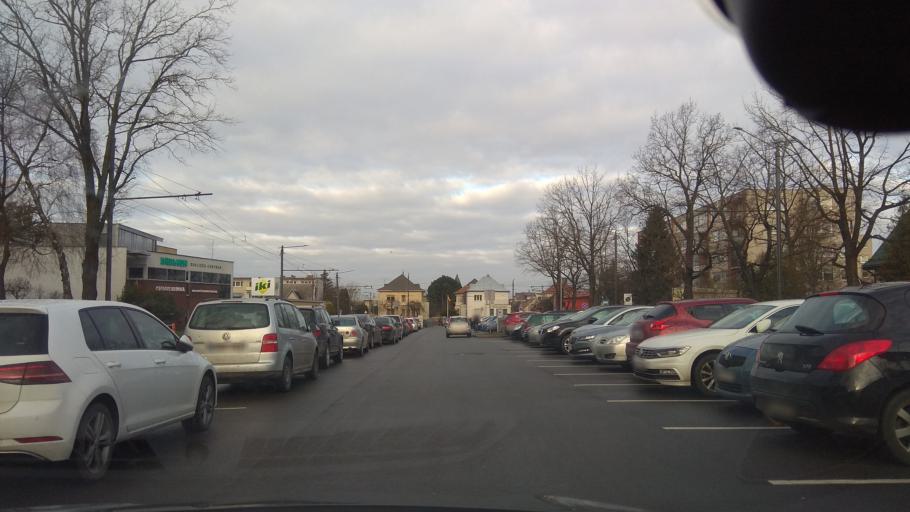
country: LT
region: Kauno apskritis
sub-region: Kaunas
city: Eiguliai
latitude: 54.9139
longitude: 23.9226
